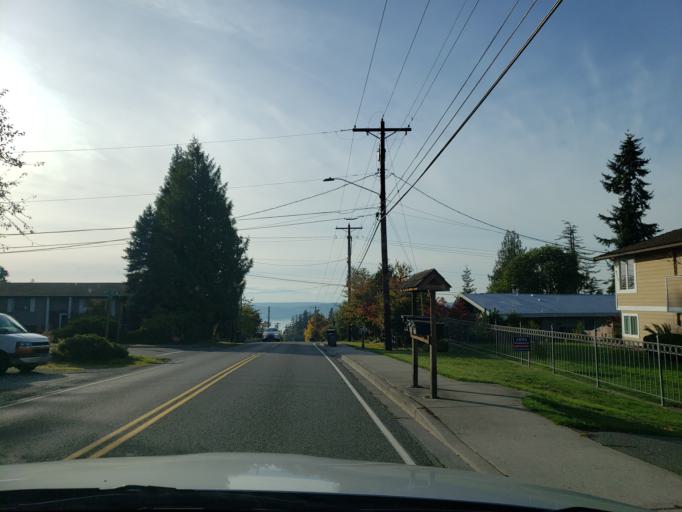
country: US
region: Washington
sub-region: Snohomish County
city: Mukilteo
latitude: 47.9294
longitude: -122.2950
